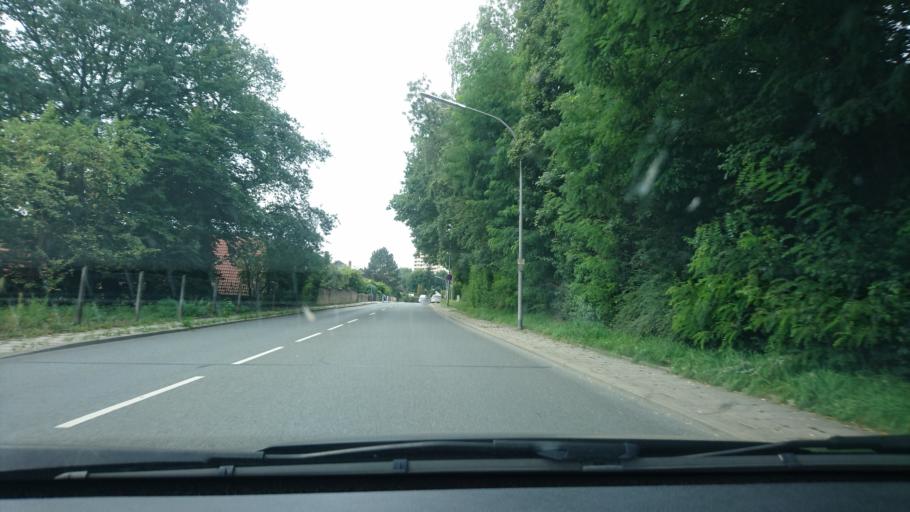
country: DE
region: Bavaria
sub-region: Upper Franconia
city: Bayreuth
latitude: 49.9400
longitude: 11.5498
